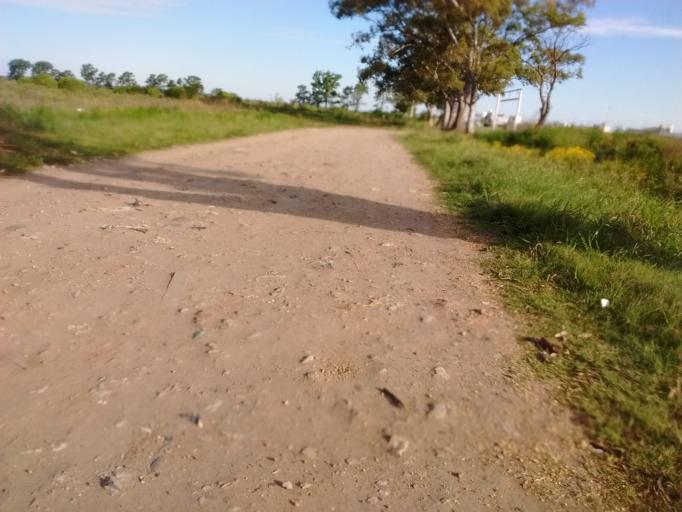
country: AR
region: Santa Fe
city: Funes
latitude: -32.8981
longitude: -60.7961
